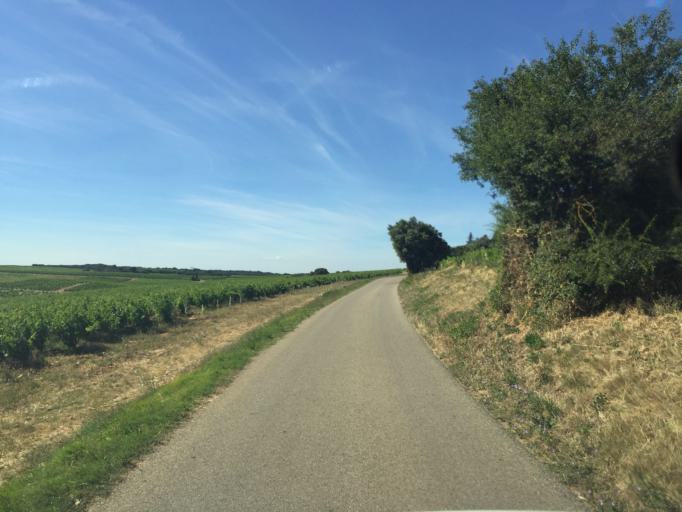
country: FR
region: Provence-Alpes-Cote d'Azur
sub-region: Departement du Vaucluse
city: Chateauneuf-du-Pape
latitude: 44.0645
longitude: 4.8106
